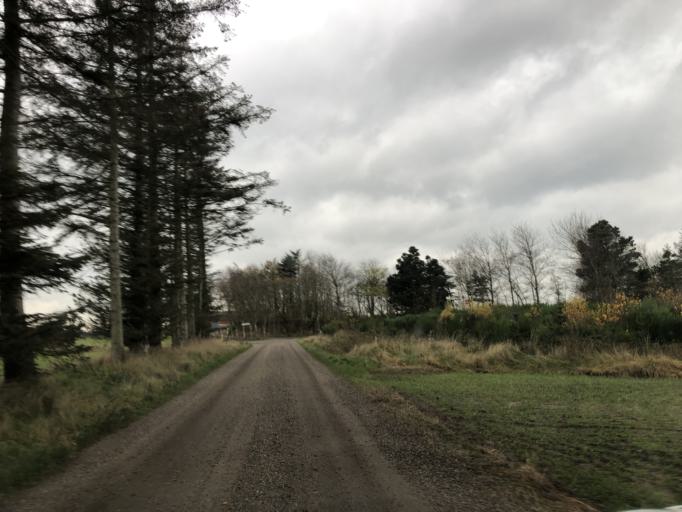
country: DK
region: Central Jutland
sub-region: Holstebro Kommune
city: Ulfborg
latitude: 56.3051
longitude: 8.1997
